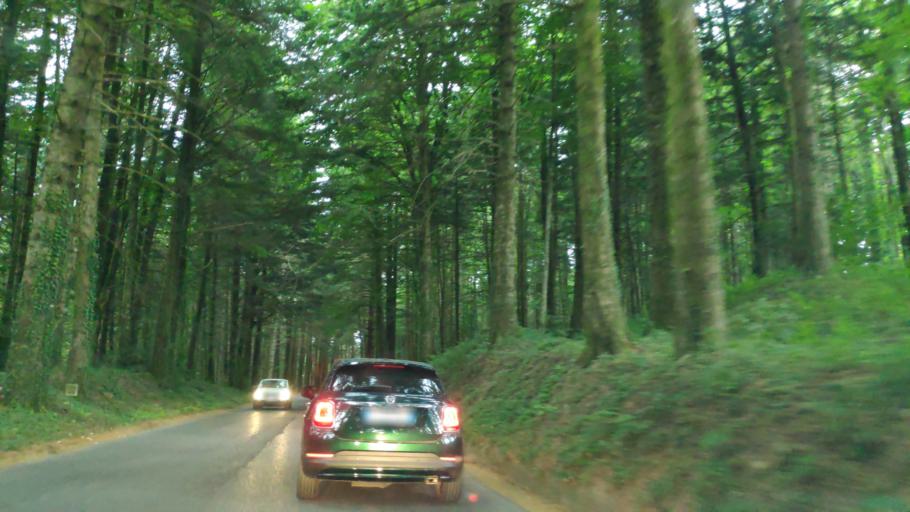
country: IT
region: Calabria
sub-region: Provincia di Vibo-Valentia
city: Mongiana
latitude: 38.5389
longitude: 16.3160
